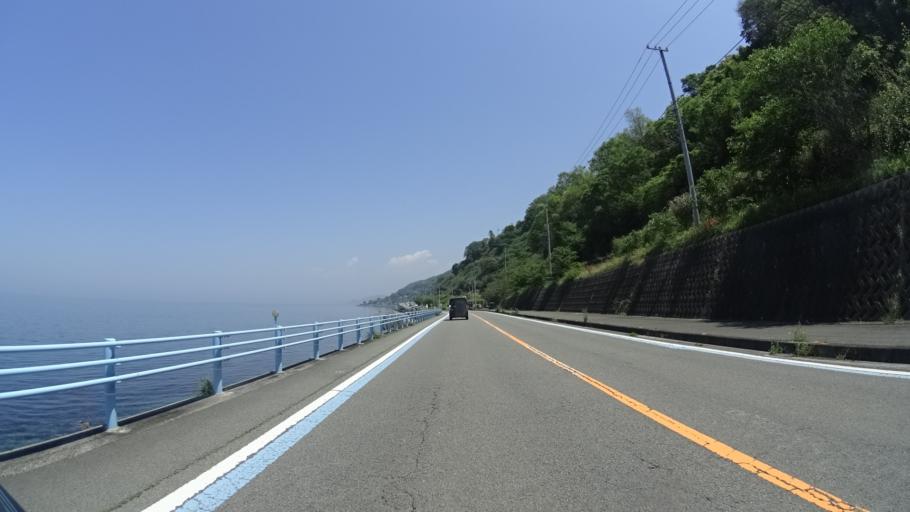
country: JP
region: Ehime
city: Iyo
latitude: 33.6617
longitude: 132.5996
